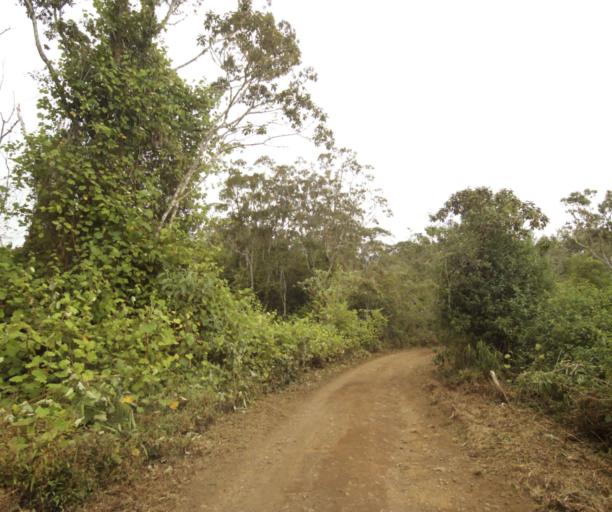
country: RE
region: Reunion
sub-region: Reunion
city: La Possession
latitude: -21.0126
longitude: 55.3600
